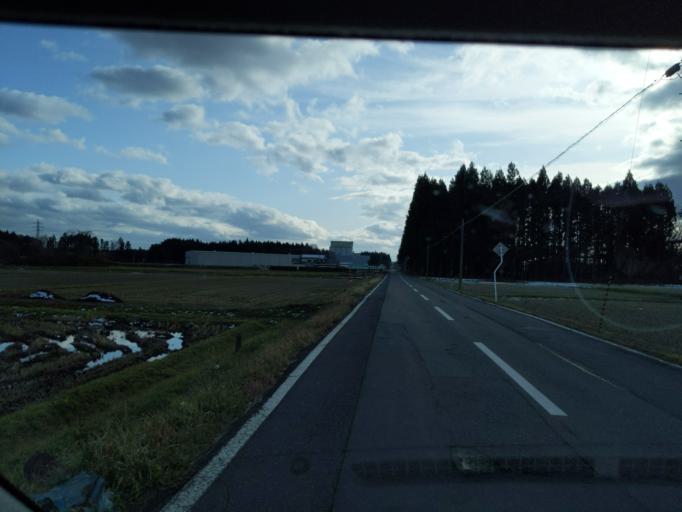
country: JP
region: Iwate
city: Mizusawa
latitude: 39.1096
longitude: 141.0822
